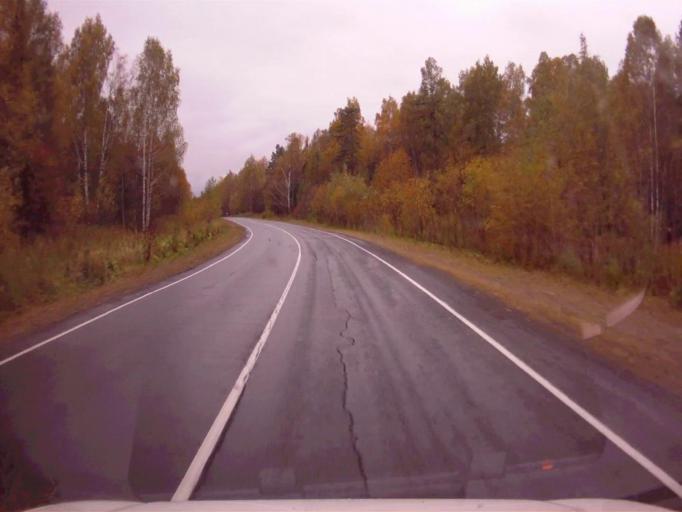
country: RU
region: Chelyabinsk
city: Nizhniy Ufaley
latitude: 56.0665
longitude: 60.0054
